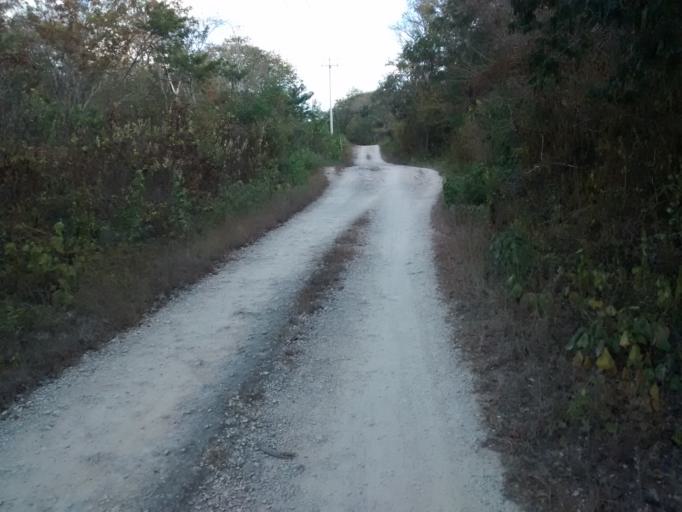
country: MX
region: Yucatan
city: Chichimila
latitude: 20.4495
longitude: -88.2019
